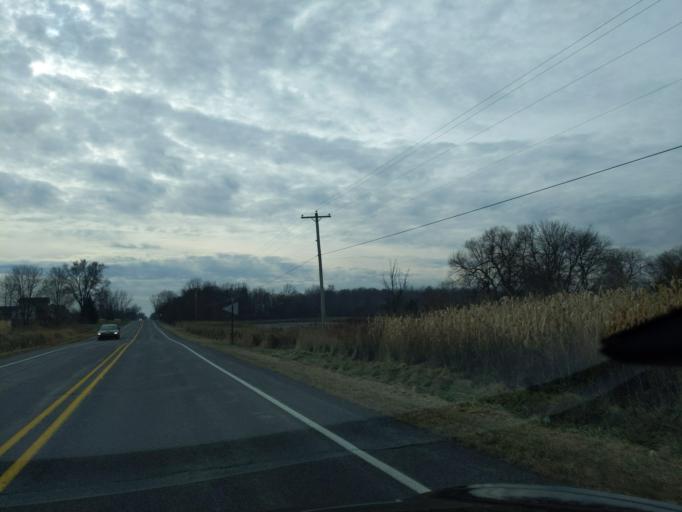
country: US
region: Michigan
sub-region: Ingham County
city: Holt
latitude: 42.5937
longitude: -84.5230
